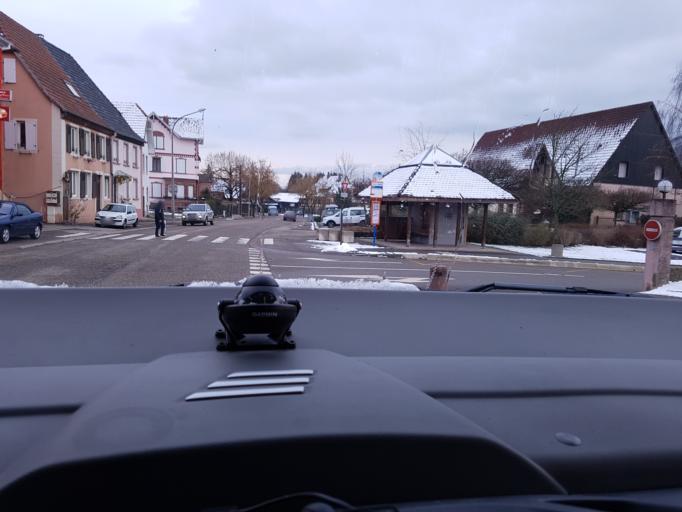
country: FR
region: Alsace
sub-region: Departement du Bas-Rhin
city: Ville
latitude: 48.3428
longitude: 7.3078
